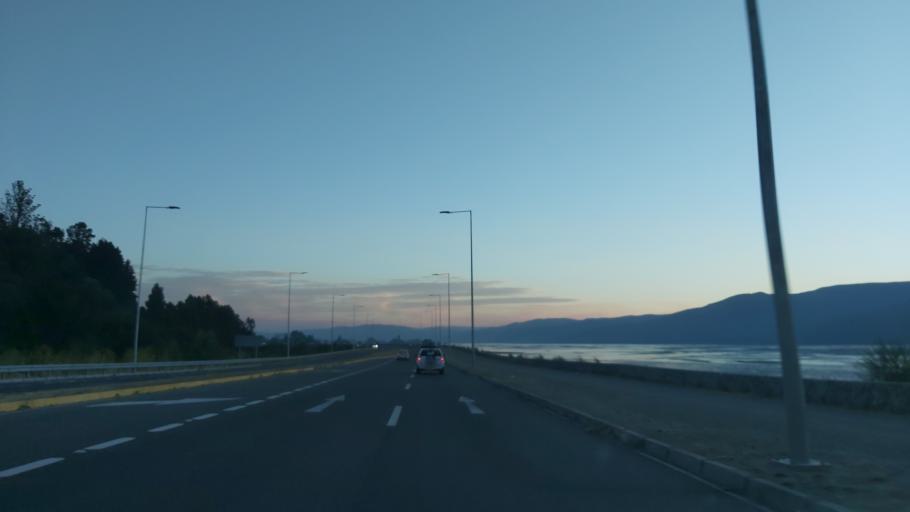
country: CL
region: Biobio
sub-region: Provincia de Concepcion
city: Concepcion
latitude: -36.8684
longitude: -73.0441
